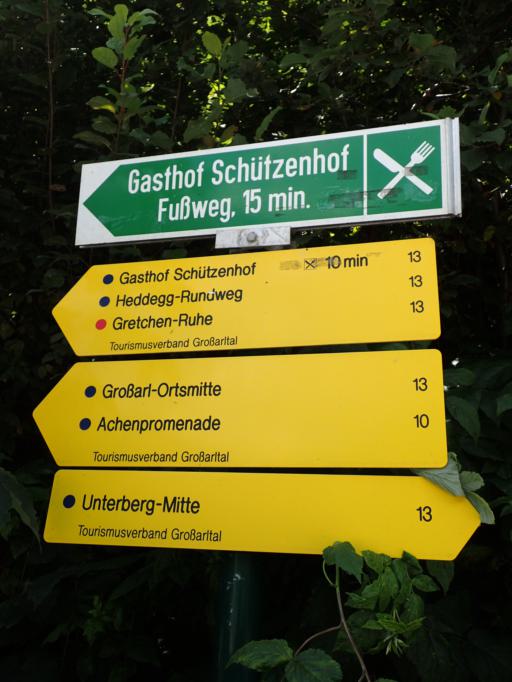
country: AT
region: Salzburg
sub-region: Politischer Bezirk Sankt Johann im Pongau
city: Huttschlag
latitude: 47.2395
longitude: 13.1962
